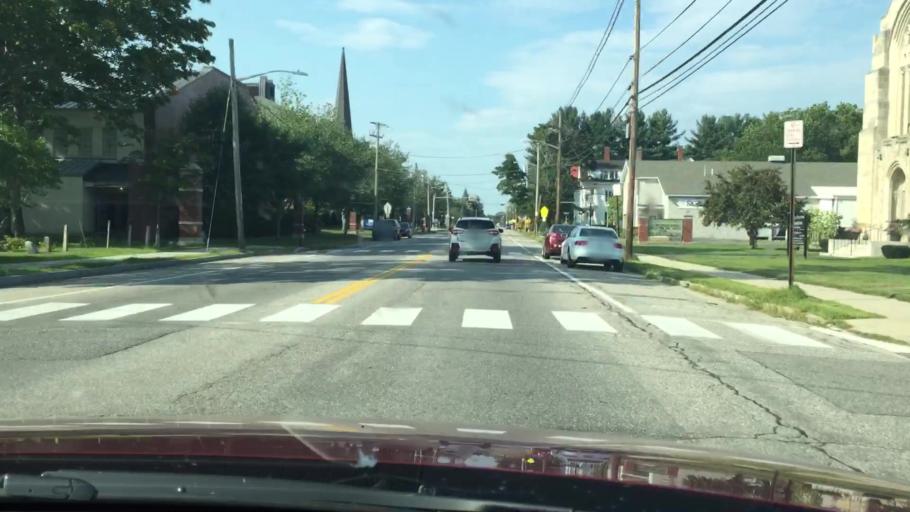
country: US
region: Maine
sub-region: Cumberland County
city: Portland
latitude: 43.6814
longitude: -70.2941
